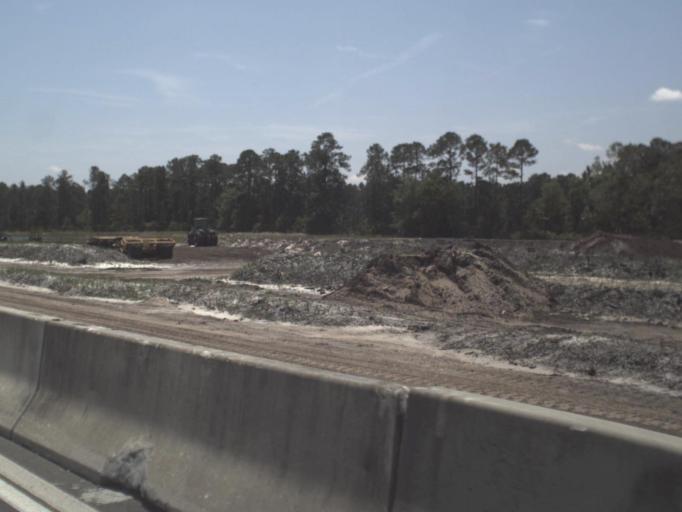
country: US
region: Florida
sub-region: Saint Johns County
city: Fruit Cove
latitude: 30.1112
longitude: -81.5109
